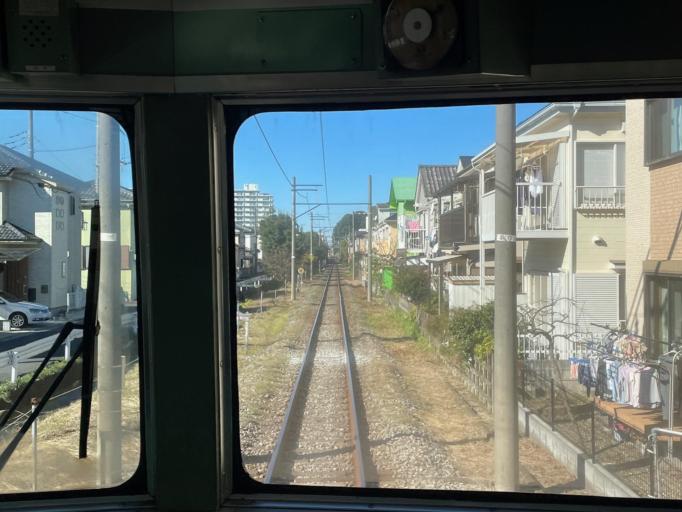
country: JP
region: Chiba
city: Nagareyama
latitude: 35.8388
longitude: 139.9134
